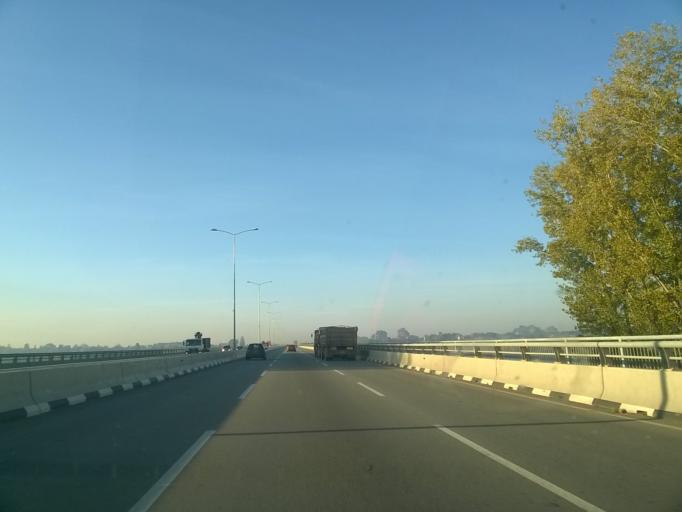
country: RS
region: Central Serbia
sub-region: Belgrade
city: Zemun
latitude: 44.8676
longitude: 20.3837
